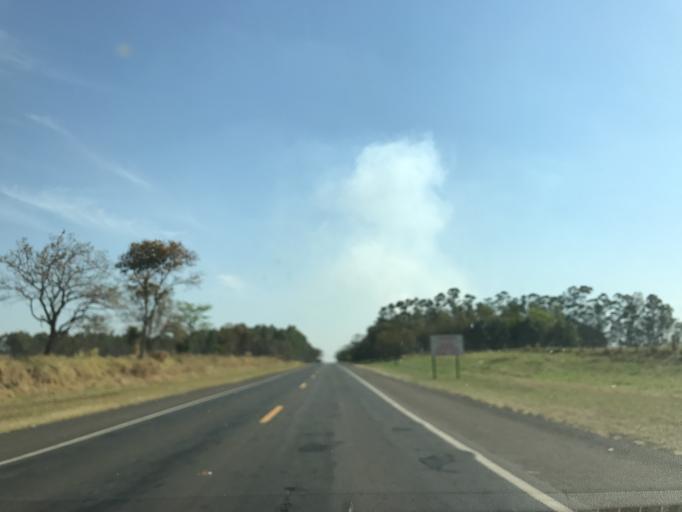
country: BR
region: Sao Paulo
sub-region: Penapolis
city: Penapolis
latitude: -21.3737
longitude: -50.0823
